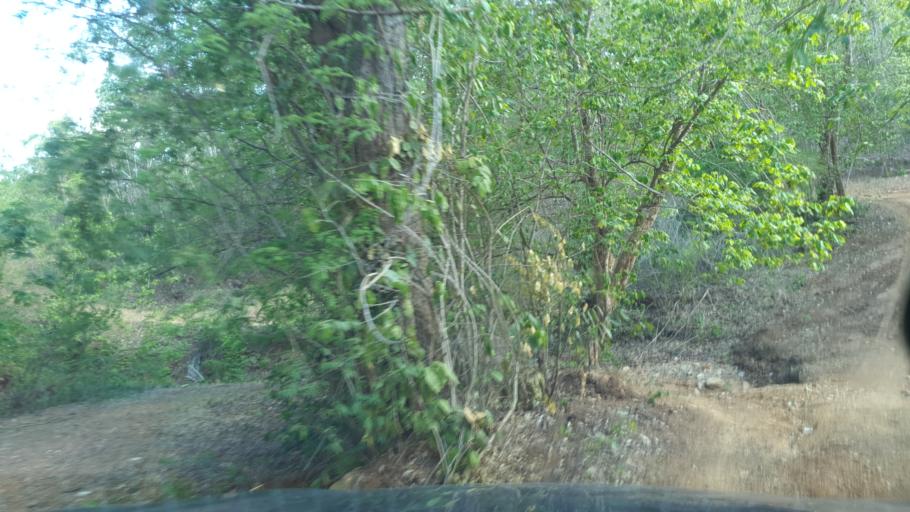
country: TH
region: Lampang
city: Sop Prap
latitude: 17.8510
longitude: 99.2843
